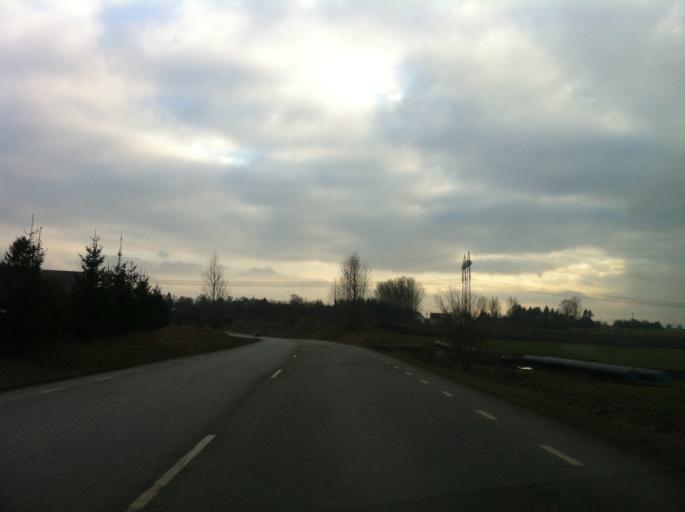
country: SE
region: Skane
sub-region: Kavlinge Kommun
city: Kaevlinge
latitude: 55.8189
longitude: 13.0906
